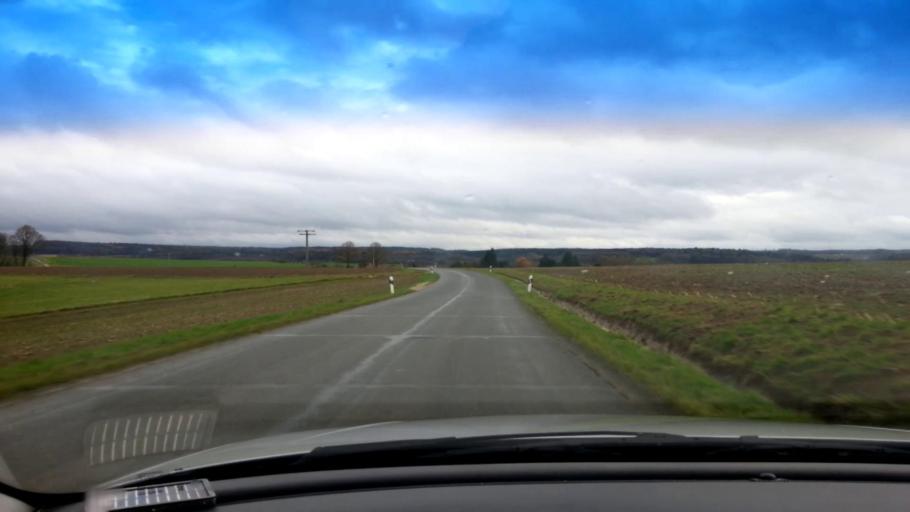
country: DE
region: Bavaria
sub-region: Upper Franconia
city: Zapfendorf
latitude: 50.0259
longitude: 10.9694
